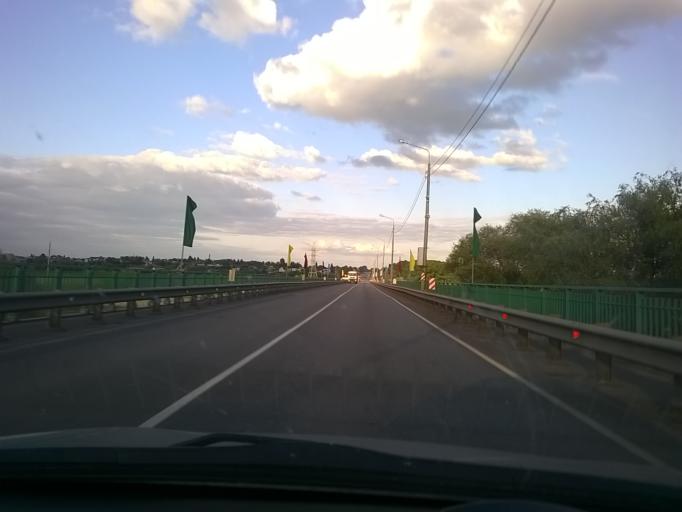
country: RU
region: Voronezj
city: Borisoglebsk
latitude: 51.3762
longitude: 42.0479
